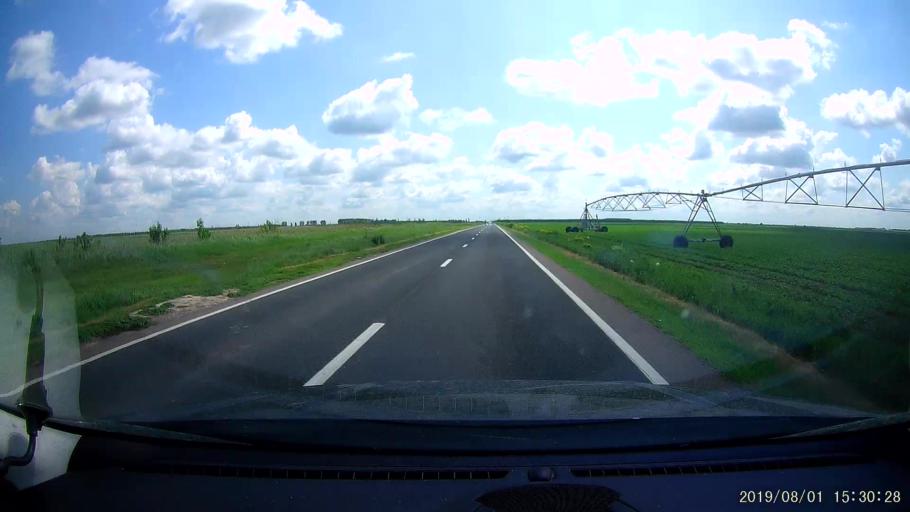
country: RO
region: Braila
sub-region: Comuna Viziru
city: Viziru
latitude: 44.9632
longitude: 27.6772
